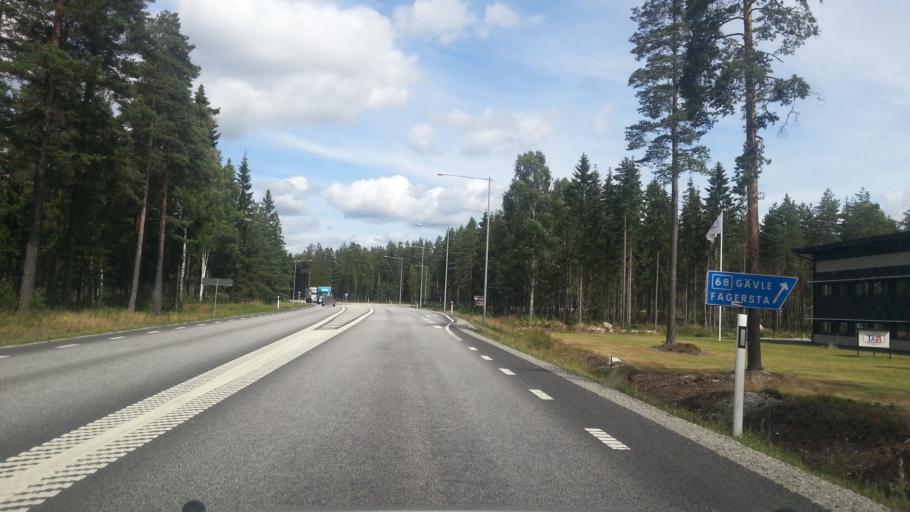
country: SE
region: OErebro
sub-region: Lindesbergs Kommun
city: Lindesberg
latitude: 59.6156
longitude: 15.1879
